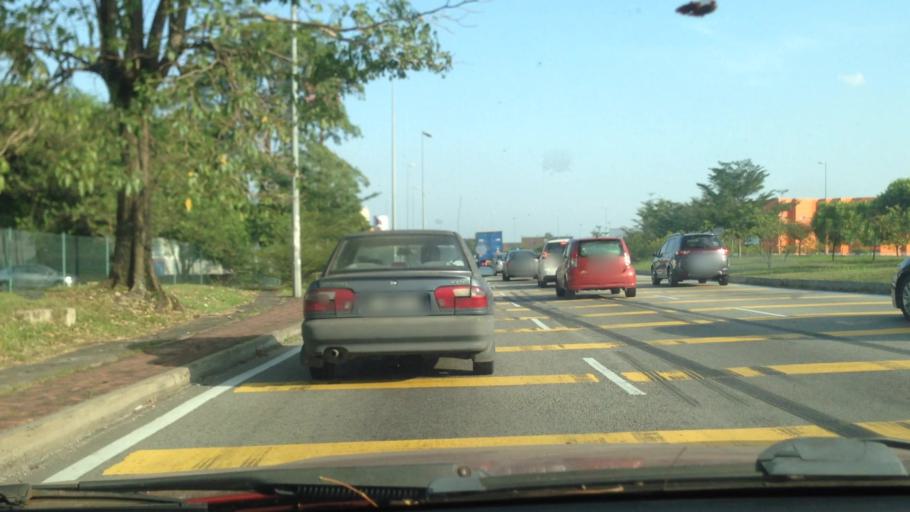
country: MY
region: Selangor
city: Subang Jaya
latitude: 3.0412
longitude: 101.5469
